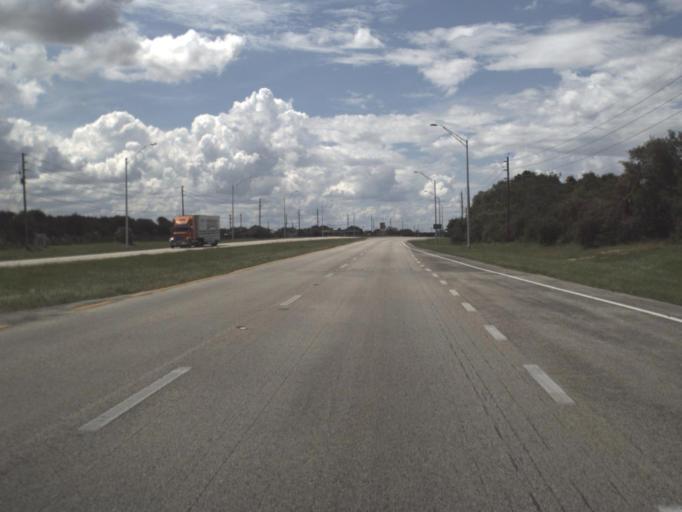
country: US
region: Florida
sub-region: Polk County
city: Babson Park
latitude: 27.8871
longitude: -81.4655
